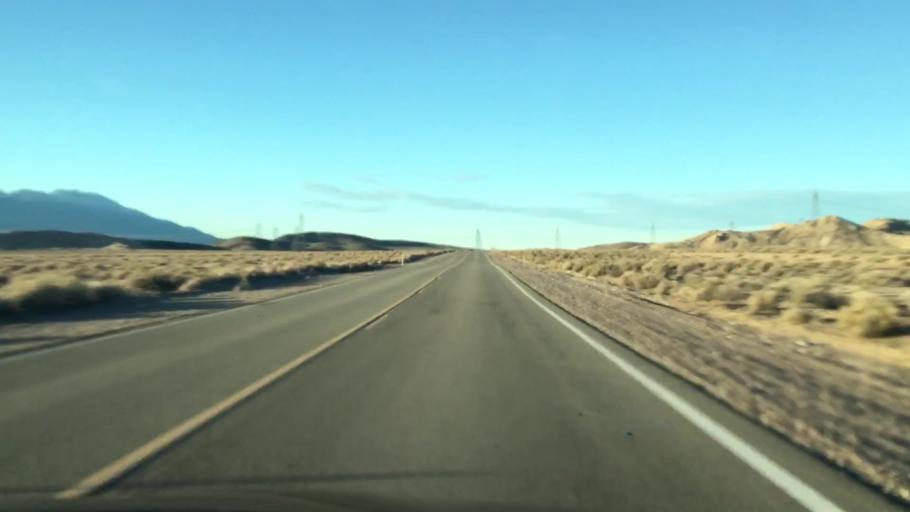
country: US
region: California
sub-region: San Bernardino County
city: Fort Irwin
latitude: 35.3773
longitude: -116.1219
